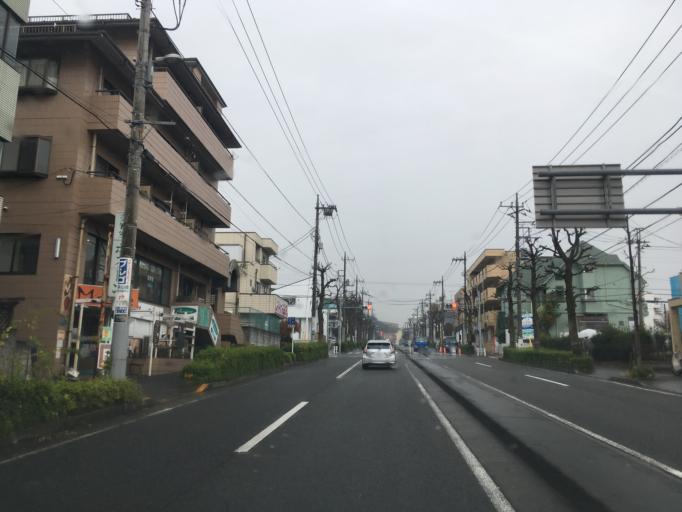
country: JP
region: Tokyo
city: Hino
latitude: 35.6352
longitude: 139.4496
